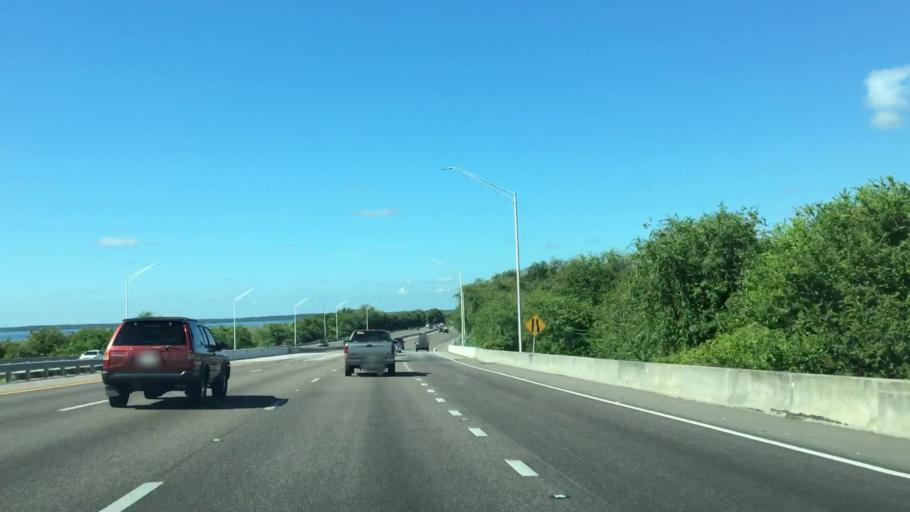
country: US
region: Florida
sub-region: Volusia County
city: DeBary
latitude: 28.8697
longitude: -81.2860
